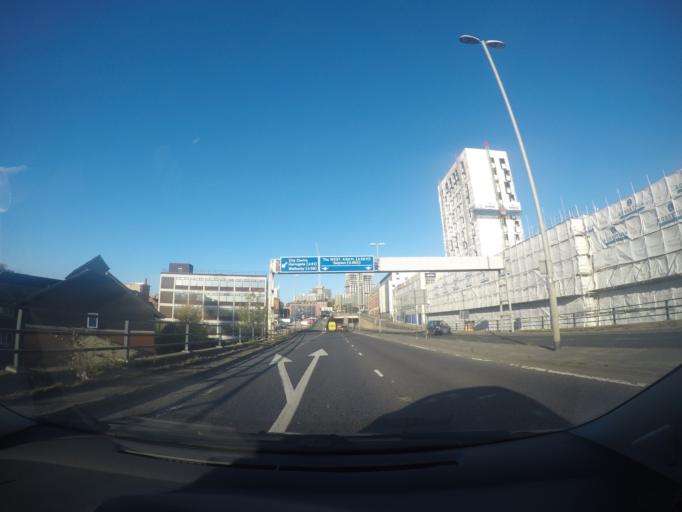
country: GB
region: England
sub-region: City and Borough of Leeds
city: Leeds
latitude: 53.8000
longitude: -1.5350
